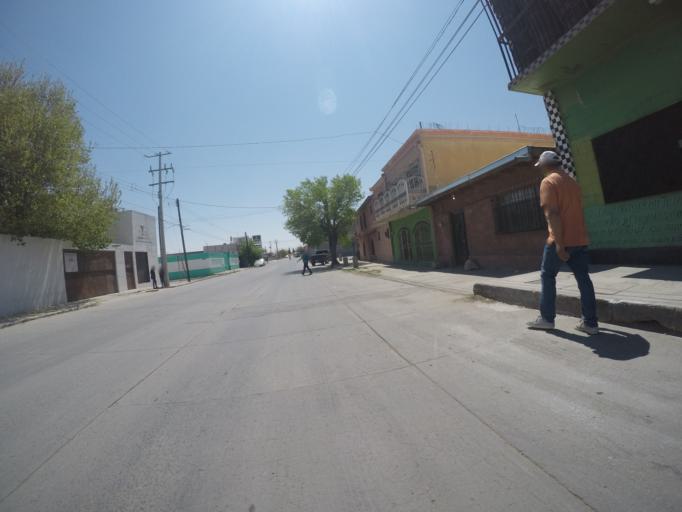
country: MX
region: Chihuahua
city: Ciudad Juarez
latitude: 31.7253
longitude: -106.4828
